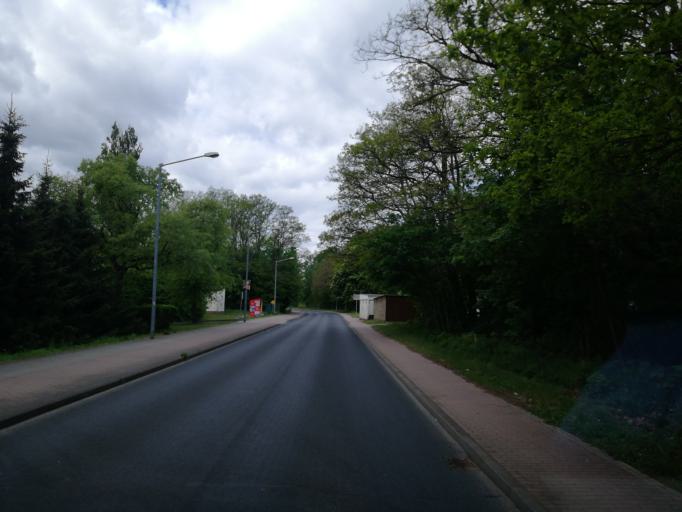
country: DE
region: Brandenburg
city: Lauchhammer
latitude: 51.5010
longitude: 13.7713
